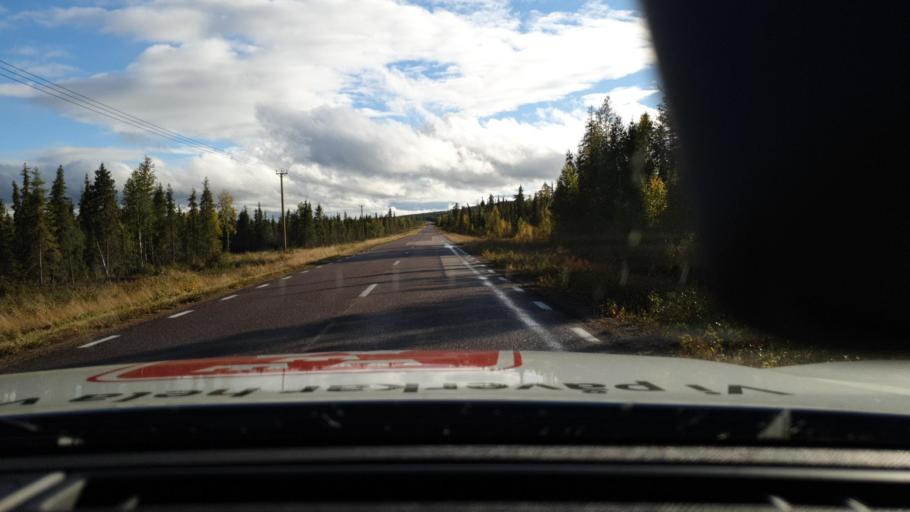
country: SE
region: Norrbotten
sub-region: Overkalix Kommun
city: OEverkalix
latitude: 66.8790
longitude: 22.7632
